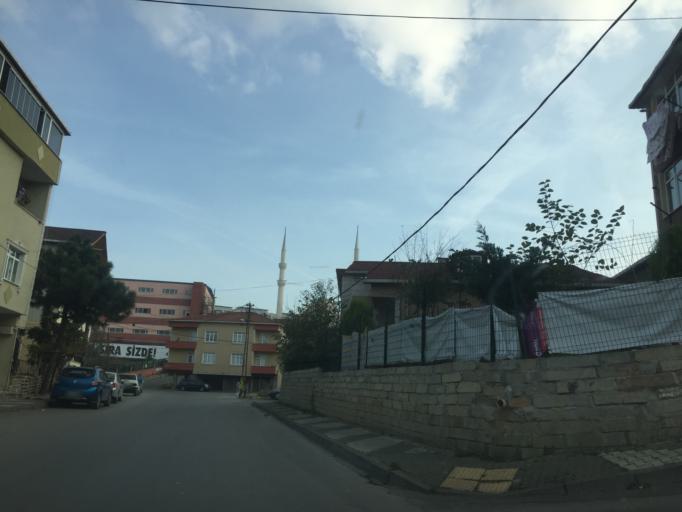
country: TR
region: Istanbul
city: Sultanbeyli
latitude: 40.9434
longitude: 29.2984
